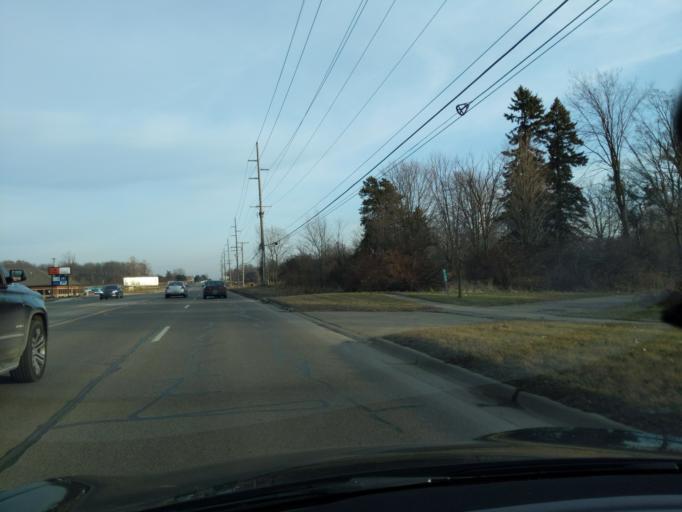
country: US
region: Michigan
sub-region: Livingston County
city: Brighton
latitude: 42.5732
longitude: -83.8303
